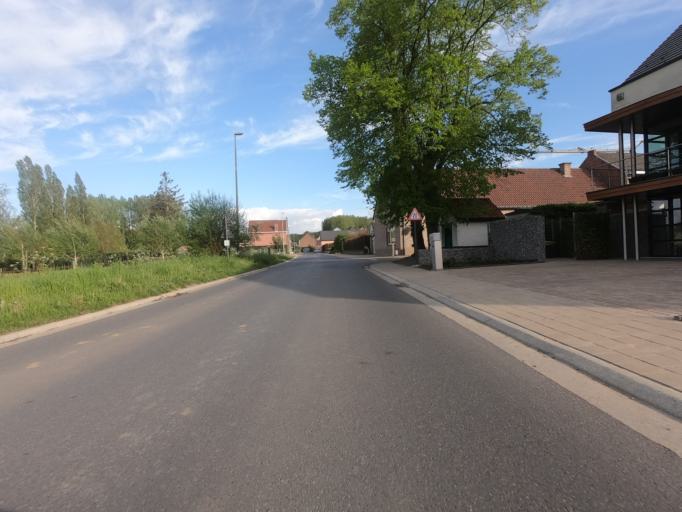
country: BE
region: Flanders
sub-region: Provincie Vlaams-Brabant
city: Galmaarden
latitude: 50.7991
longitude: 3.9729
